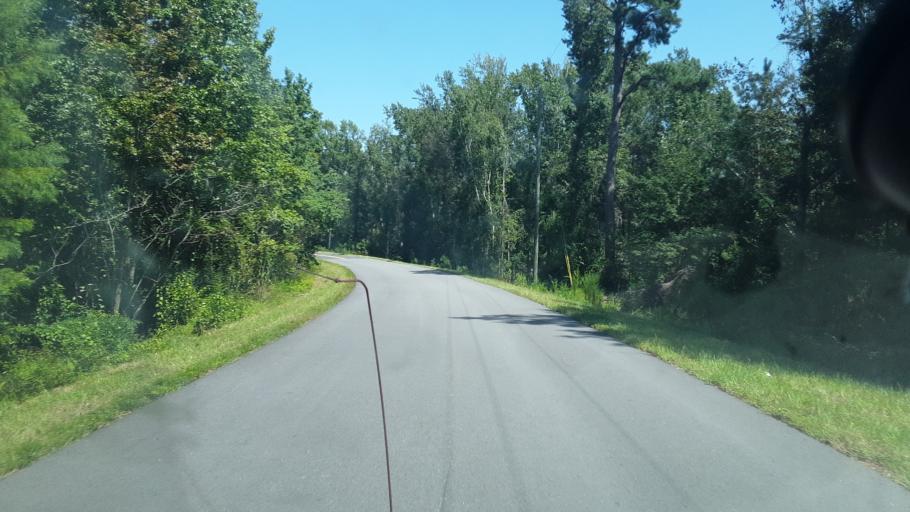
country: US
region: South Carolina
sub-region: Orangeburg County
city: Edisto
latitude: 33.5790
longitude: -81.0373
